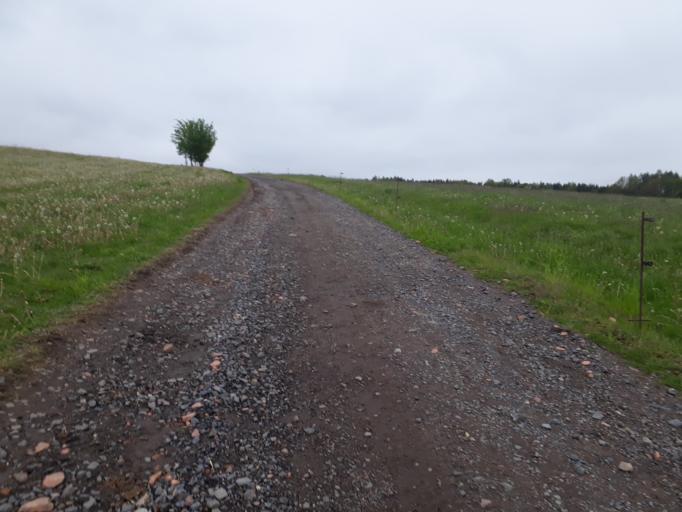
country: DE
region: Saxony
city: Reinhardtsgrimma
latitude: 50.8870
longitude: 13.7533
